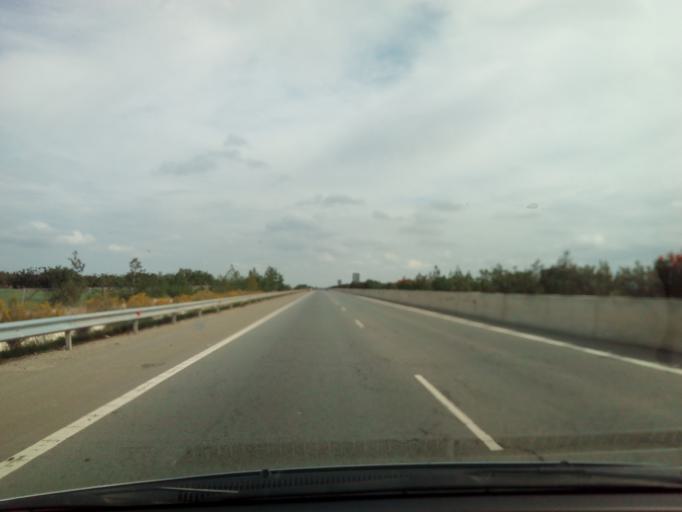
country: CY
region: Lefkosia
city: Kokkinotrimithia
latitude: 35.1616
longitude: 33.1709
